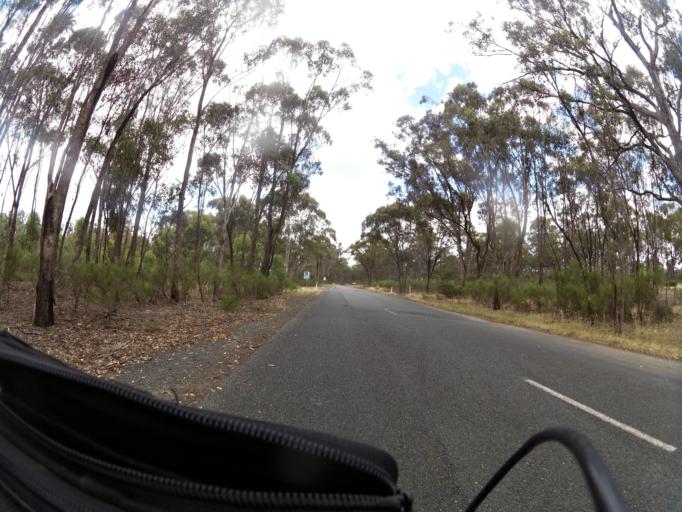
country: AU
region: Victoria
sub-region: Greater Shepparton
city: Shepparton
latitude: -36.6899
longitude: 145.1780
